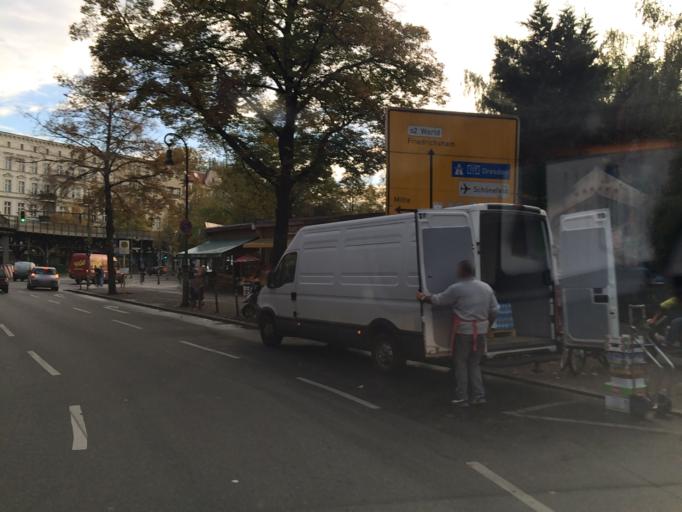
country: DE
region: Berlin
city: Berlin Treptow
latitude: 52.5006
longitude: 13.4414
